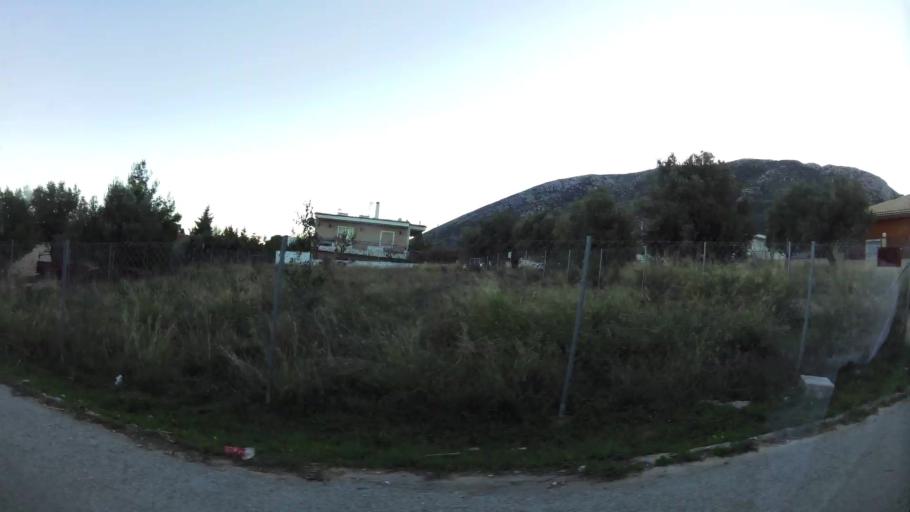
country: GR
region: Attica
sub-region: Nomarchia Anatolikis Attikis
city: Paiania
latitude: 37.9711
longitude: 23.8404
